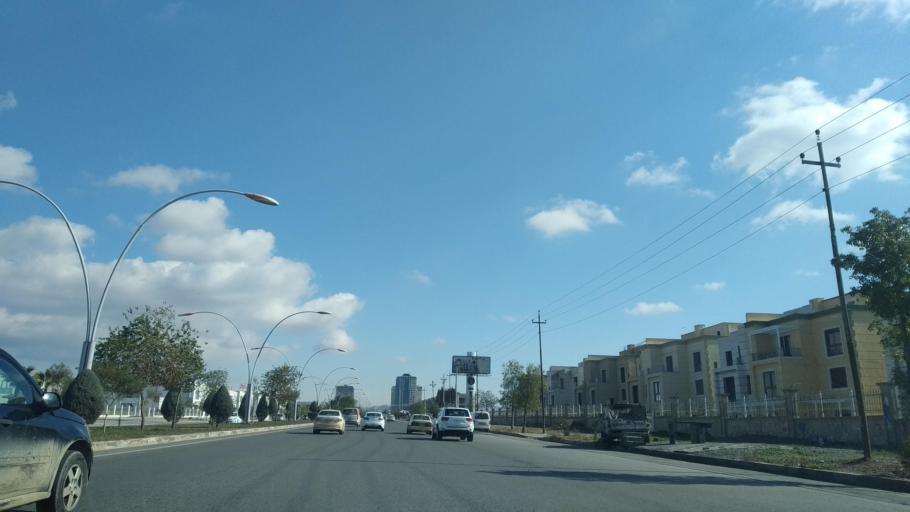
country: IQ
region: Arbil
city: Erbil
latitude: 36.2027
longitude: 44.1062
